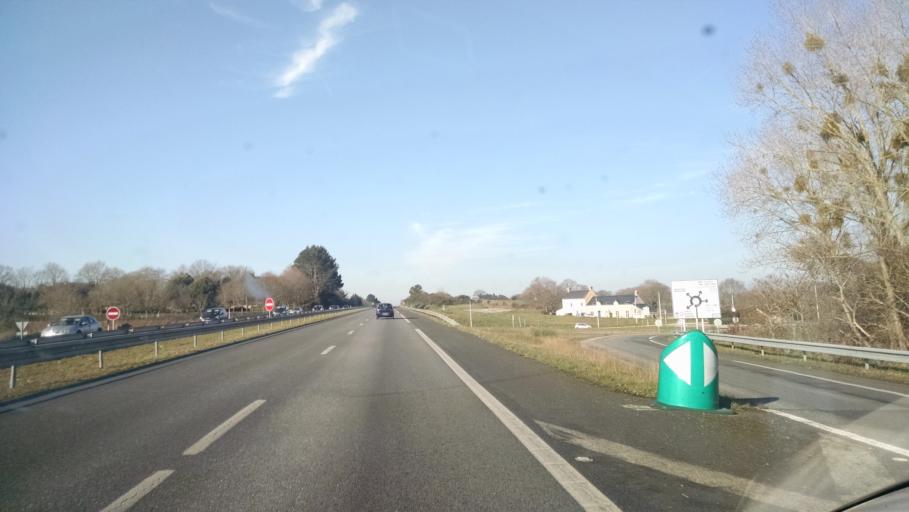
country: FR
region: Brittany
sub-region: Departement du Morbihan
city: Theix
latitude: 47.6316
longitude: -2.6466
